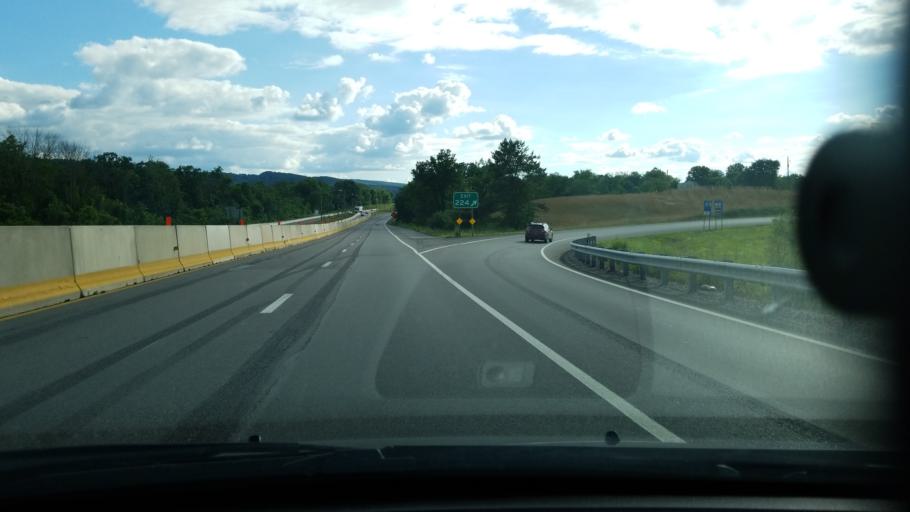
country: US
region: Pennsylvania
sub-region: Northumberland County
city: Riverside
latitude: 40.9954
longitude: -76.6465
